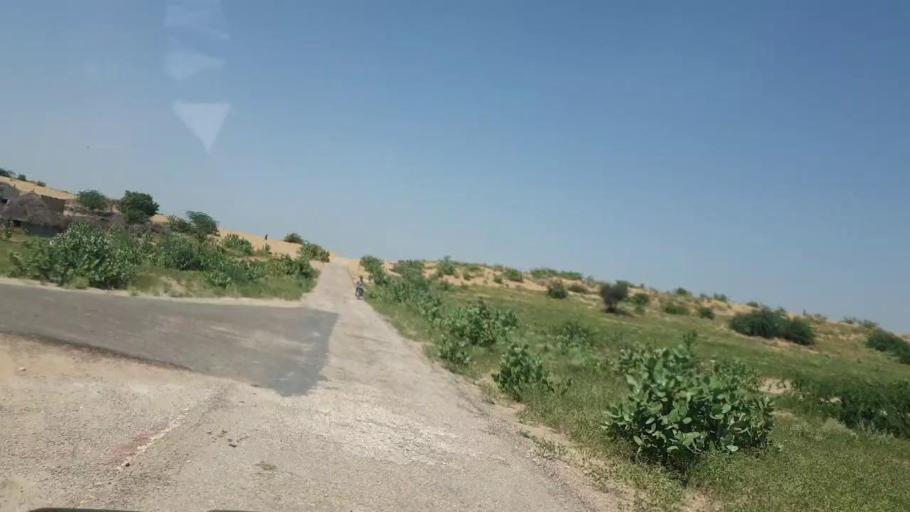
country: PK
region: Sindh
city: Chor
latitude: 25.3526
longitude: 70.3425
